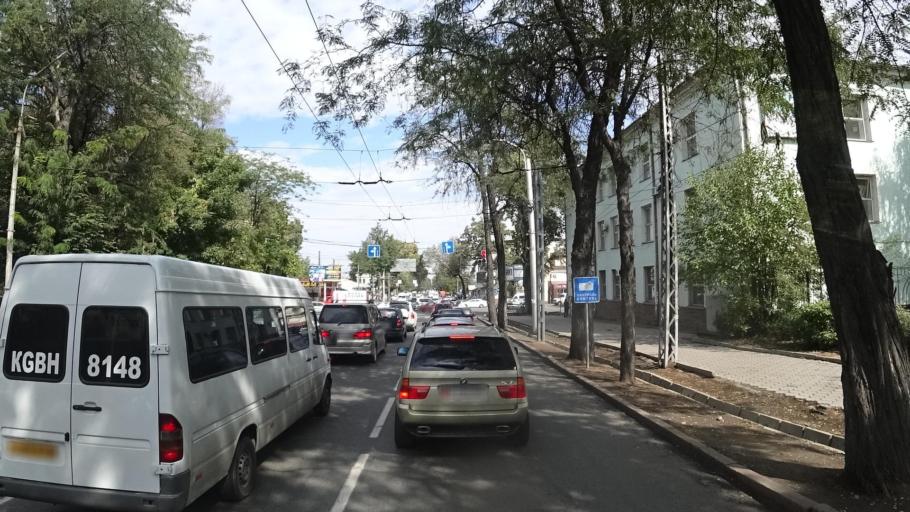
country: KG
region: Chuy
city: Bishkek
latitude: 42.8842
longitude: 74.6119
